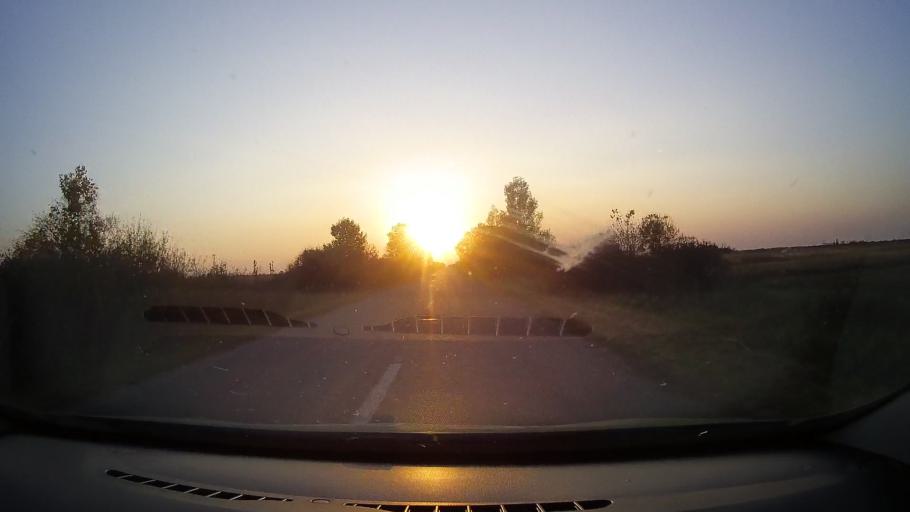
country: RO
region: Arad
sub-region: Comuna Seleus
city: Seleus
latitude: 46.3834
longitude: 21.6894
